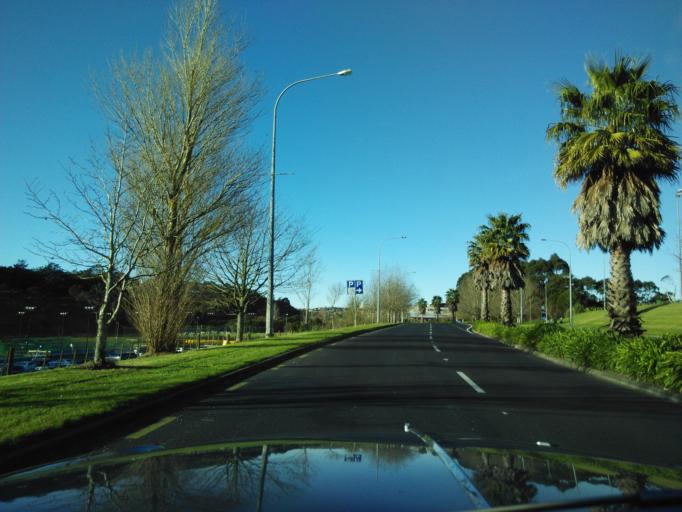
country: NZ
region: Auckland
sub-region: Auckland
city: Rothesay Bay
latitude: -36.7248
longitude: 174.6997
